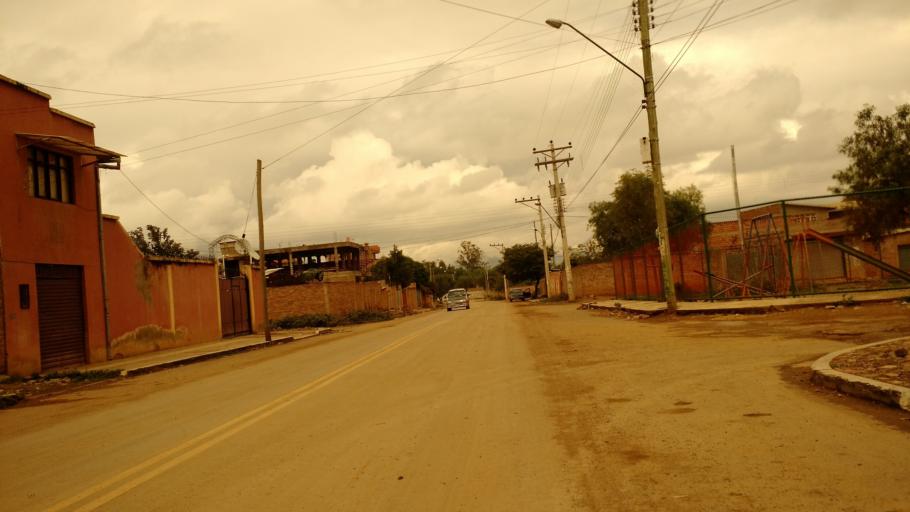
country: BO
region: Cochabamba
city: Cochabamba
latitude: -17.4494
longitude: -66.1533
